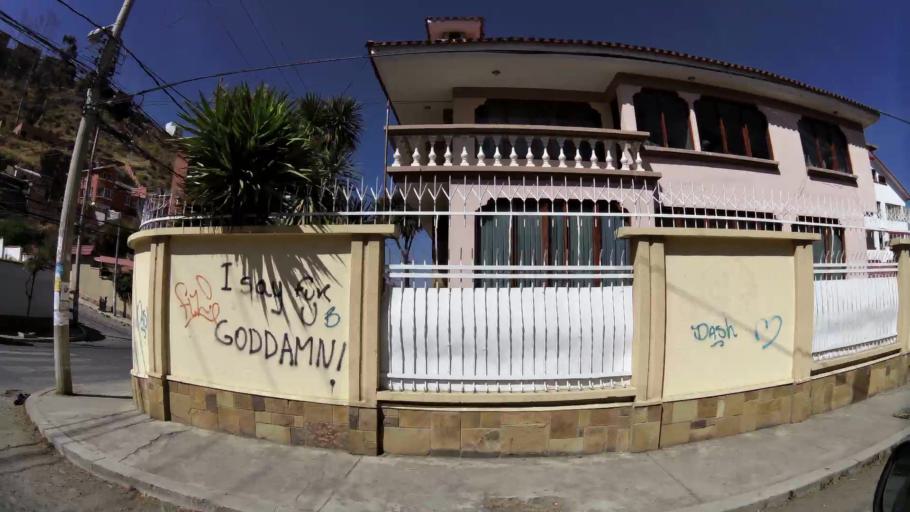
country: BO
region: La Paz
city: La Paz
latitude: -16.5117
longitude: -68.0855
